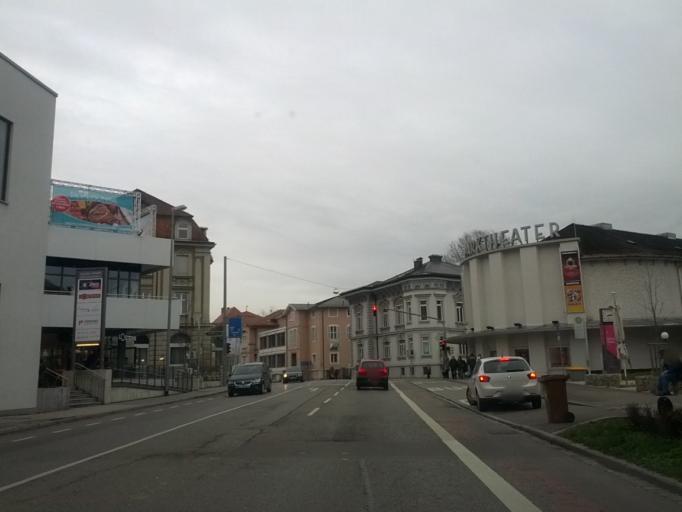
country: DE
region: Bavaria
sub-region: Swabia
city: Kempten (Allgaeu)
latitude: 47.7243
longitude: 10.3154
